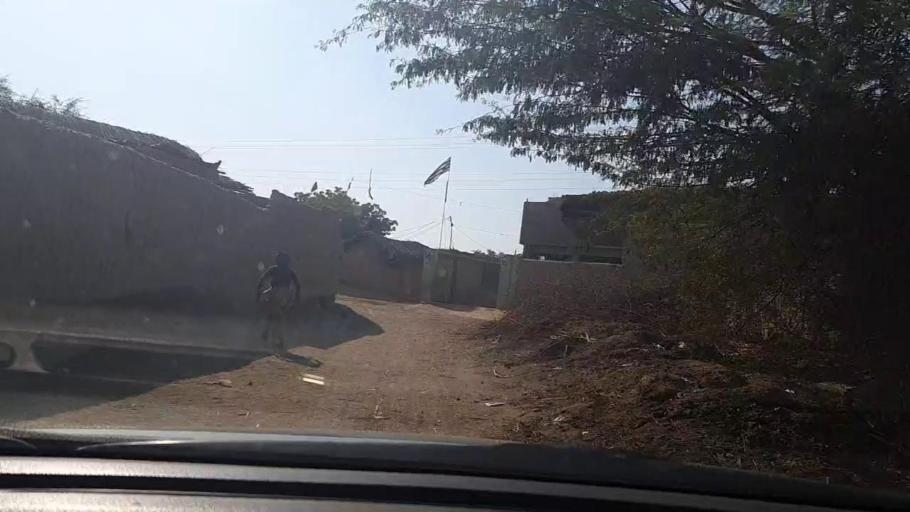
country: PK
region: Sindh
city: Sann
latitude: 26.2683
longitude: 68.0710
